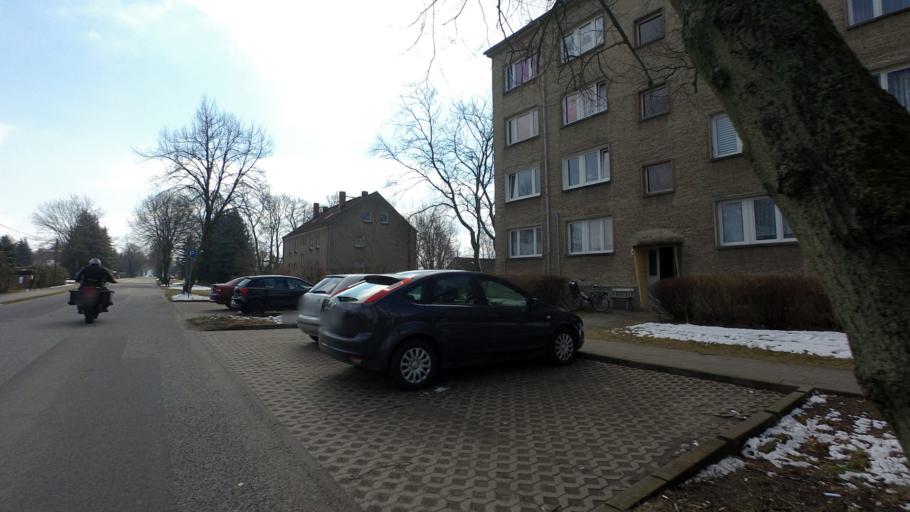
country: DE
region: Brandenburg
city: Rudnitz
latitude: 52.6994
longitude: 13.6551
